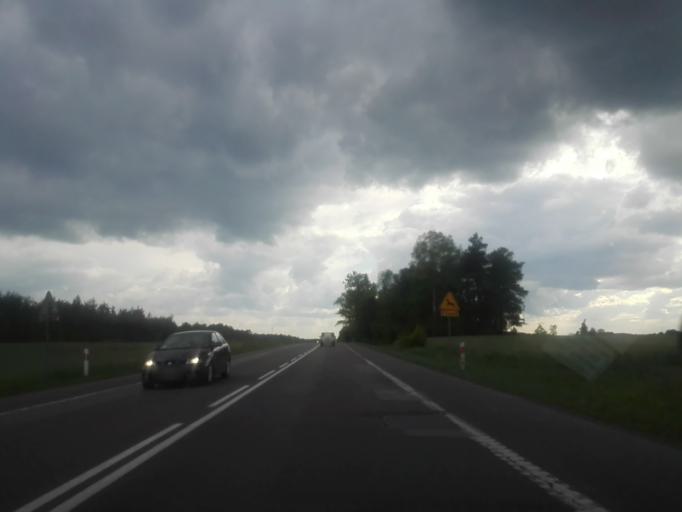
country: PL
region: Podlasie
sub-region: Powiat zambrowski
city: Szumowo
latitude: 52.9040
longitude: 22.0855
